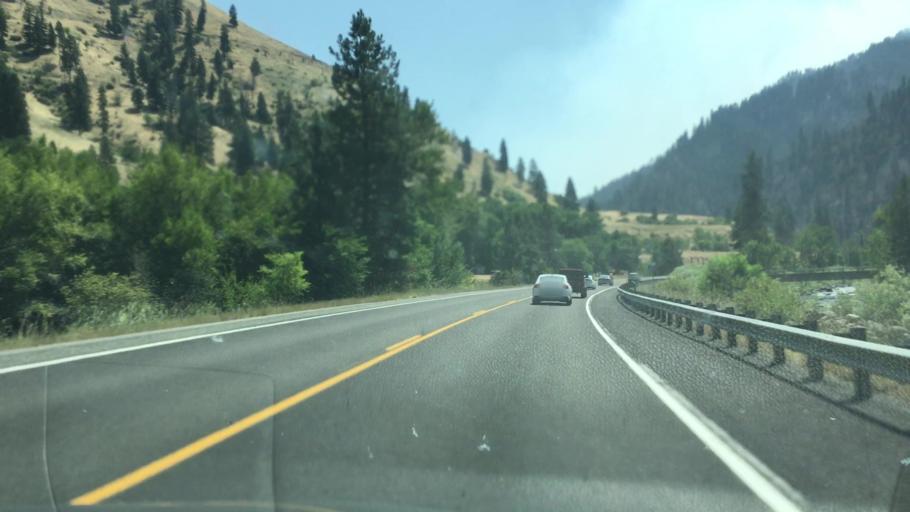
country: US
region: Idaho
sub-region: Valley County
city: McCall
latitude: 45.2798
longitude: -116.3456
